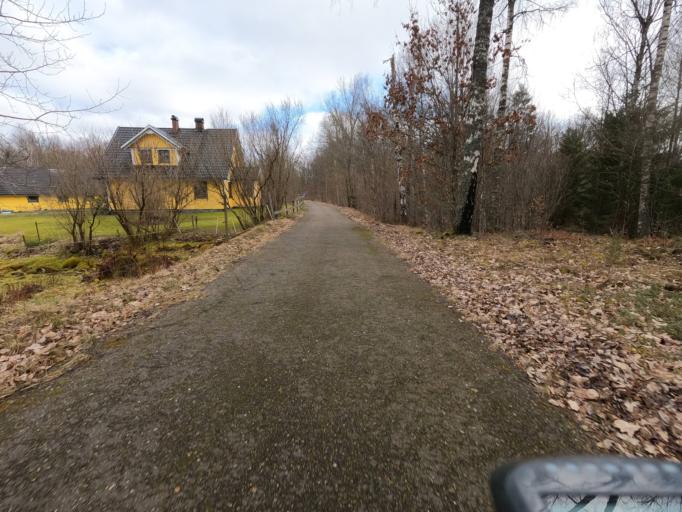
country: SE
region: Joenkoeping
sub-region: Varnamo Kommun
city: Rydaholm
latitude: 56.8349
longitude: 14.2451
